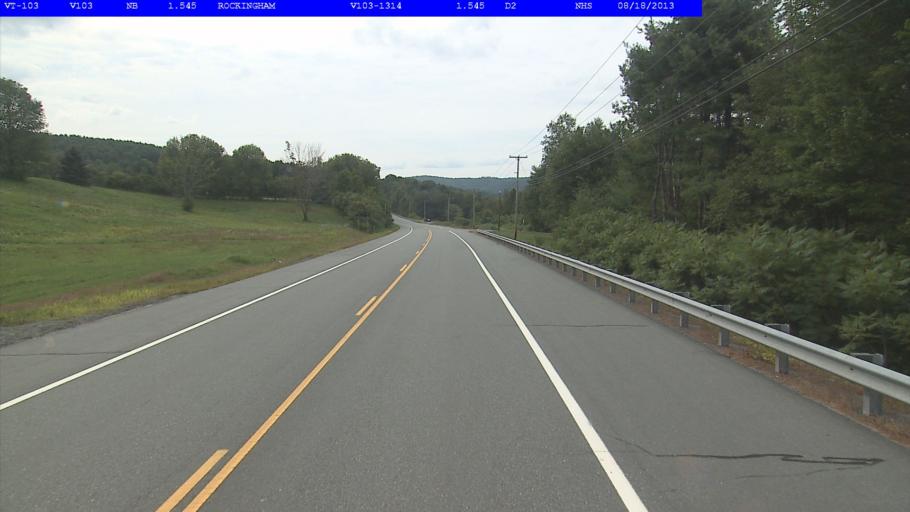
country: US
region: Vermont
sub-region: Windham County
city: Rockingham
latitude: 43.1892
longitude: -72.4850
